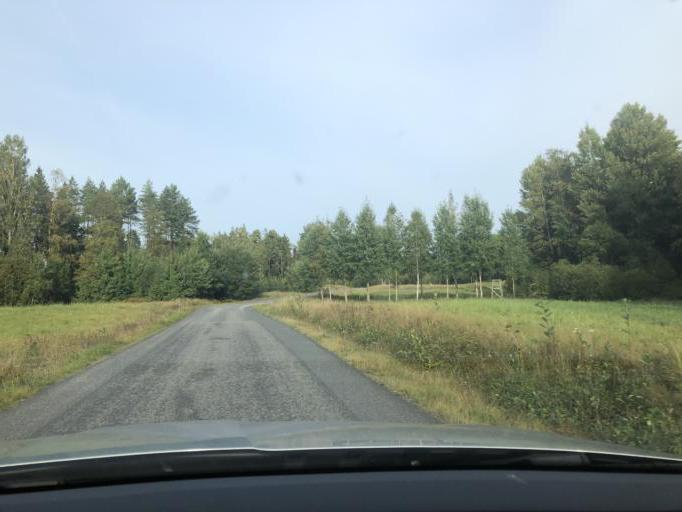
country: SE
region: Joenkoeping
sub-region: Vetlanda Kommun
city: Ekenassjon
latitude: 57.4947
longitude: 14.9006
